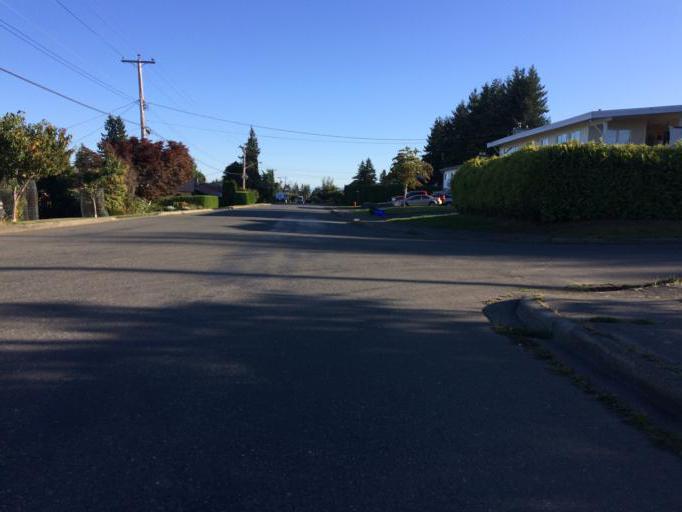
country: CA
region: British Columbia
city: Campbell River
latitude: 49.9894
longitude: -125.2307
